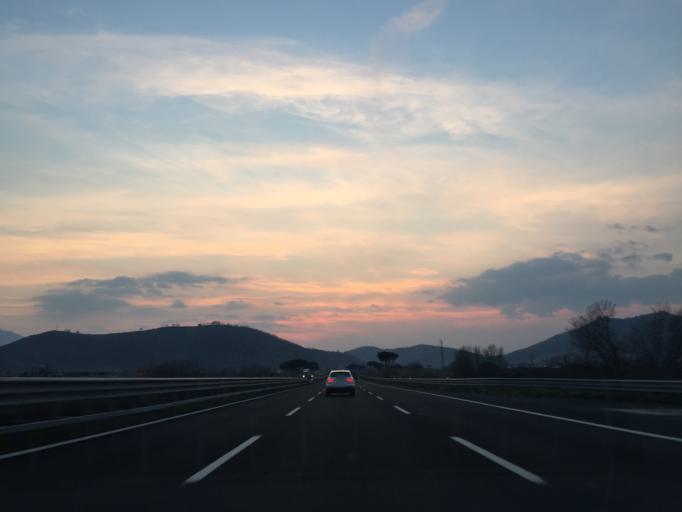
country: IT
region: Campania
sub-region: Provincia di Salerno
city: Roccapiemonte
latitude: 40.7675
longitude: 14.6919
